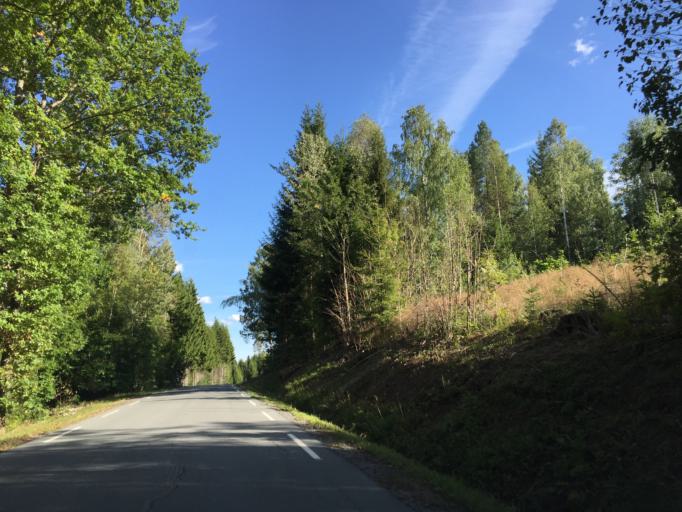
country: NO
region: Buskerud
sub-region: Ovre Eiker
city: Hokksund
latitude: 59.6602
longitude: 9.9014
